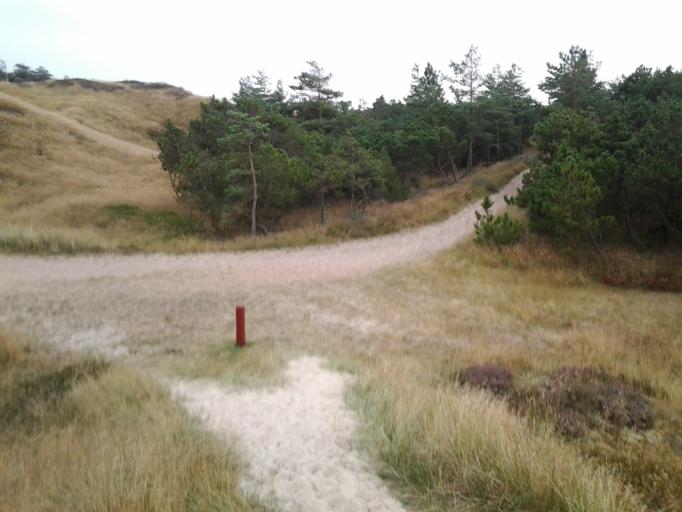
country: DE
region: Schleswig-Holstein
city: List
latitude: 55.1159
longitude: 8.5262
